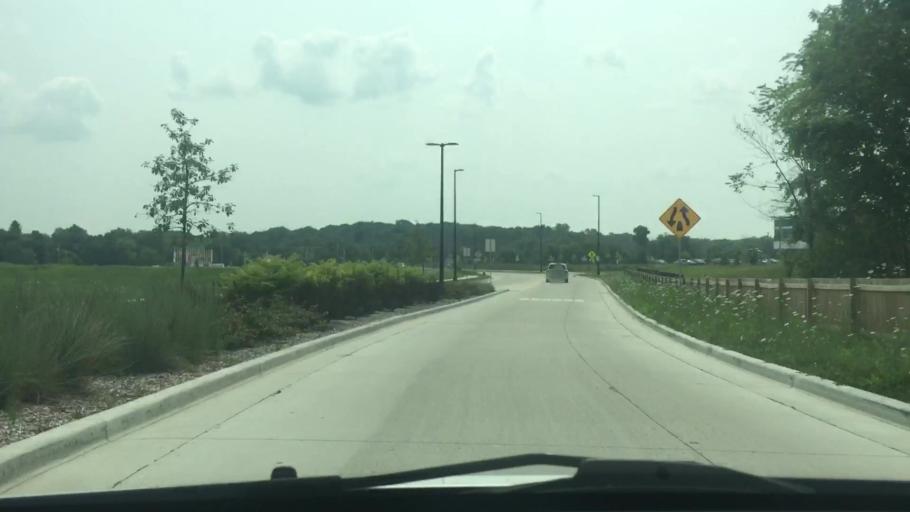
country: US
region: Wisconsin
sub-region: Milwaukee County
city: Greendale
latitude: 42.9050
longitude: -87.9408
